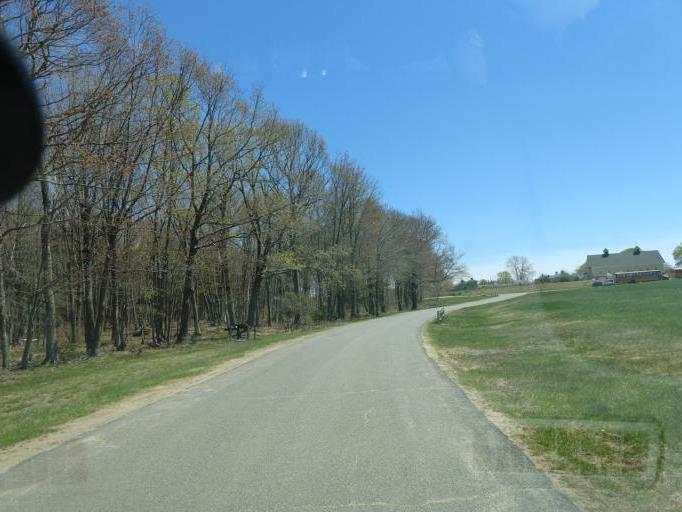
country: US
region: Maine
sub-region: York County
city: Wells Beach Station
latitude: 43.3398
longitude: -70.5523
